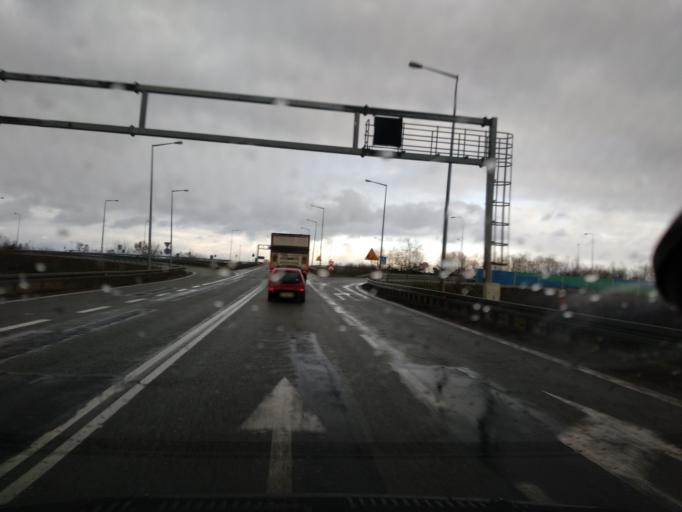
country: PL
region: Greater Poland Voivodeship
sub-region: Powiat koninski
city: Stare Miasto
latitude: 52.1604
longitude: 18.2060
